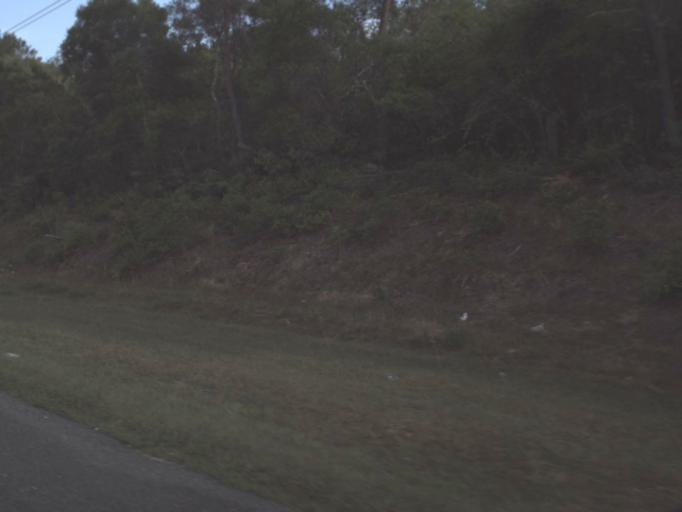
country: US
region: Florida
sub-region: Lake County
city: Astor
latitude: 29.1750
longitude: -81.6959
